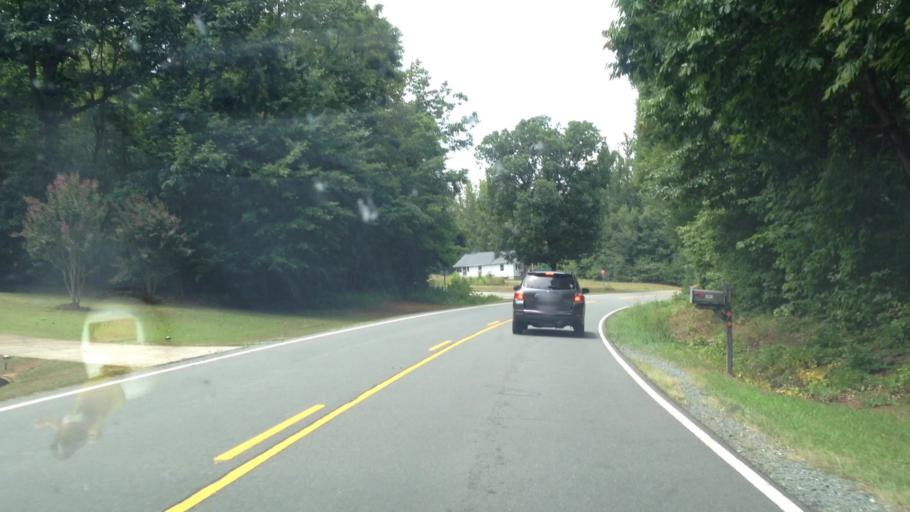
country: US
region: North Carolina
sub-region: Stokes County
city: Walnut Cove
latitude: 36.3819
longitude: -80.0948
